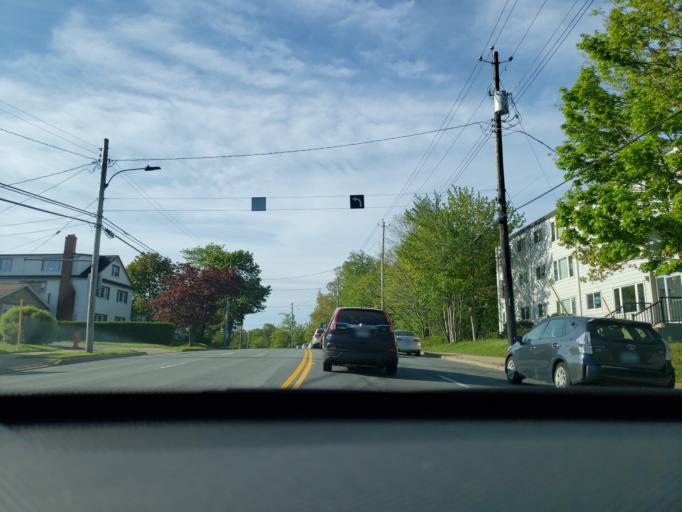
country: CA
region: Nova Scotia
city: Dartmouth
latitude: 44.6500
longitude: -63.6307
